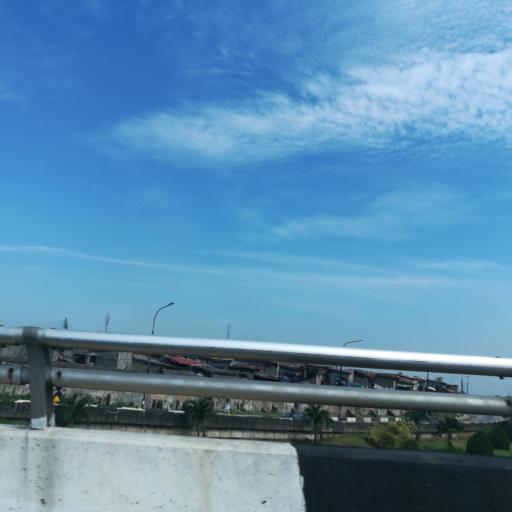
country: NG
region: Lagos
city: Lagos
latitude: 6.4601
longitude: 3.3949
